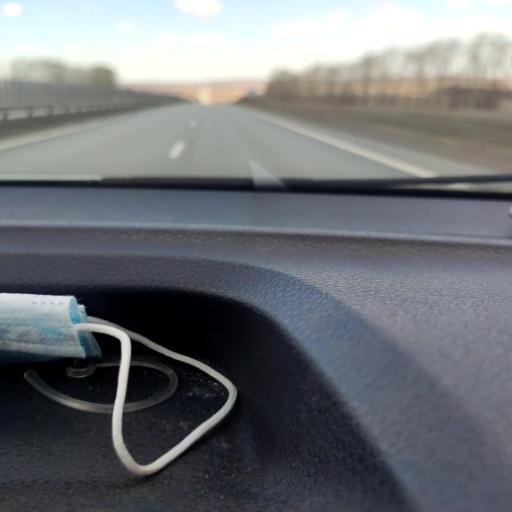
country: RU
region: Bashkortostan
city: Alekseyevka
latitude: 54.7318
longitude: 55.0399
